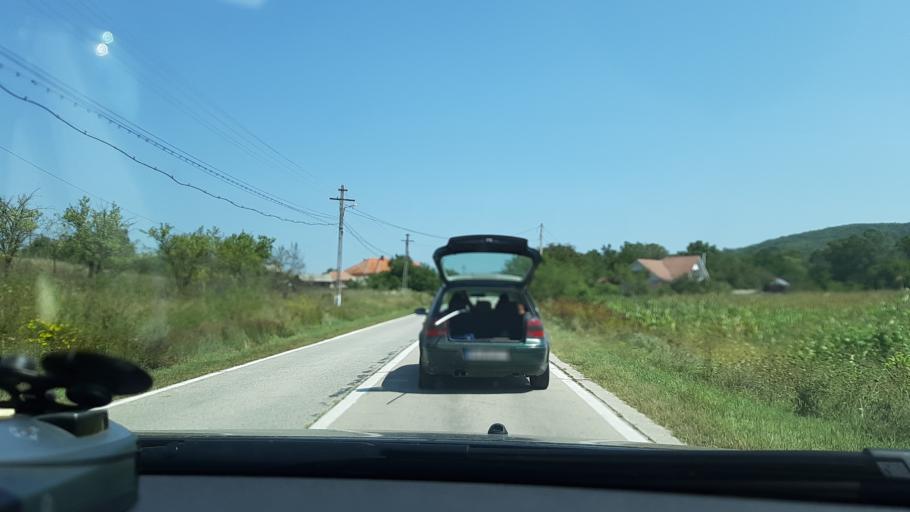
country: RO
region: Gorj
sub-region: Comuna Logresti-Mosteni
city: Logresti Mosteni
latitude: 44.8920
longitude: 23.7222
